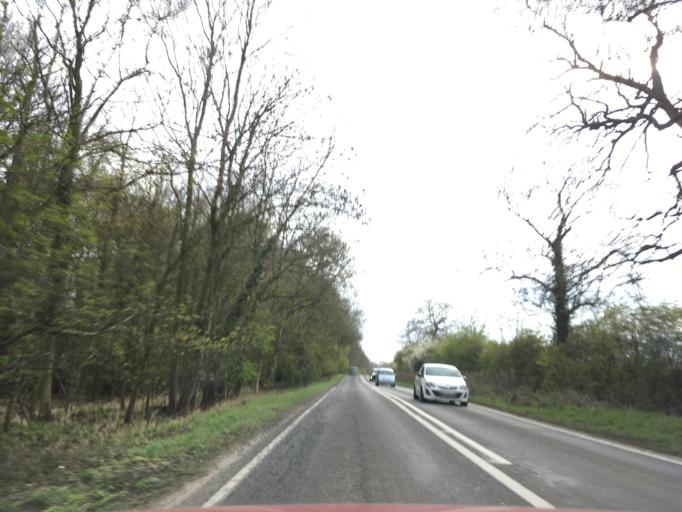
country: GB
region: England
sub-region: Oxfordshire
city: North Leigh
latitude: 51.8105
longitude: -1.4359
